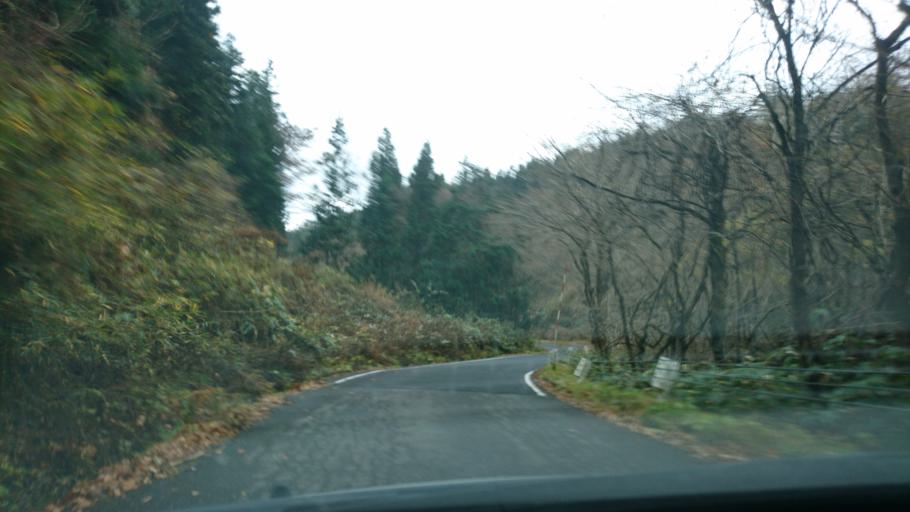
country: JP
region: Iwate
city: Ichinoseki
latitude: 38.9134
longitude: 140.9065
